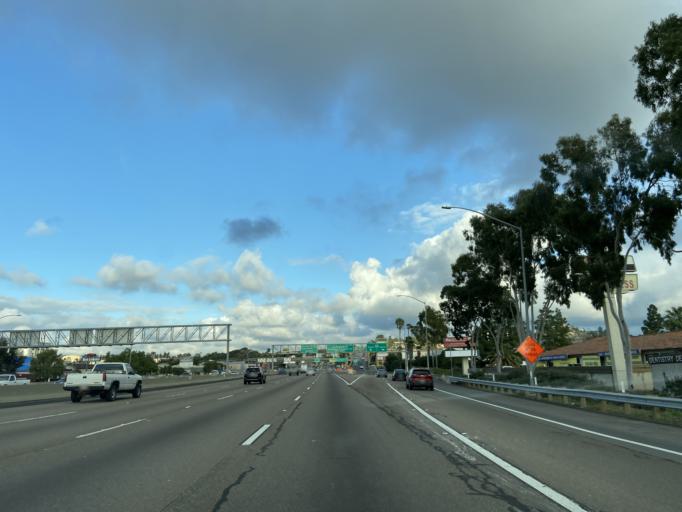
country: US
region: California
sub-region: San Diego County
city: La Mesa
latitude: 32.7744
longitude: -117.0124
